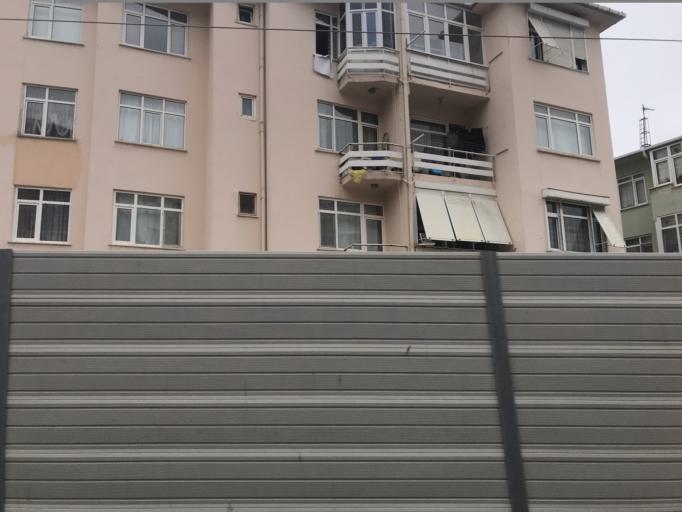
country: TR
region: Istanbul
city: Pendik
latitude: 40.8765
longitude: 29.2435
